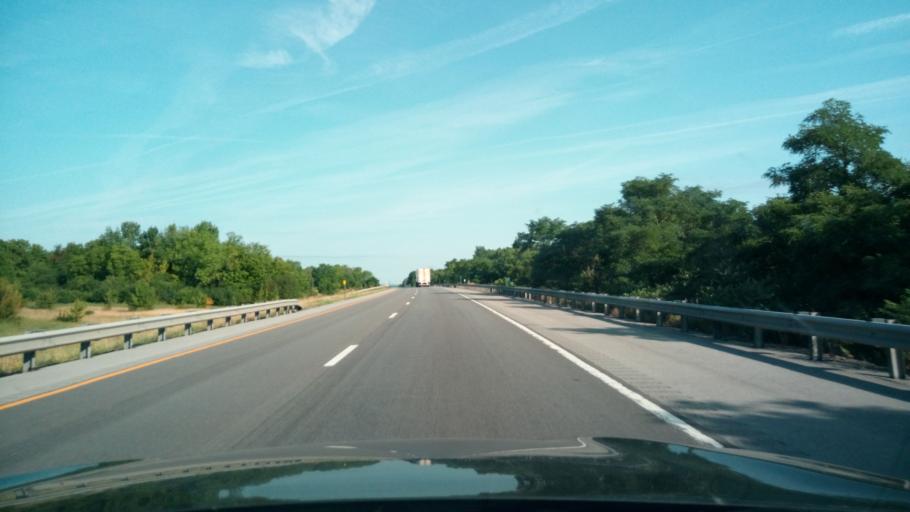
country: US
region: New York
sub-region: Livingston County
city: Mount Morris
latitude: 42.6421
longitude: -77.7892
